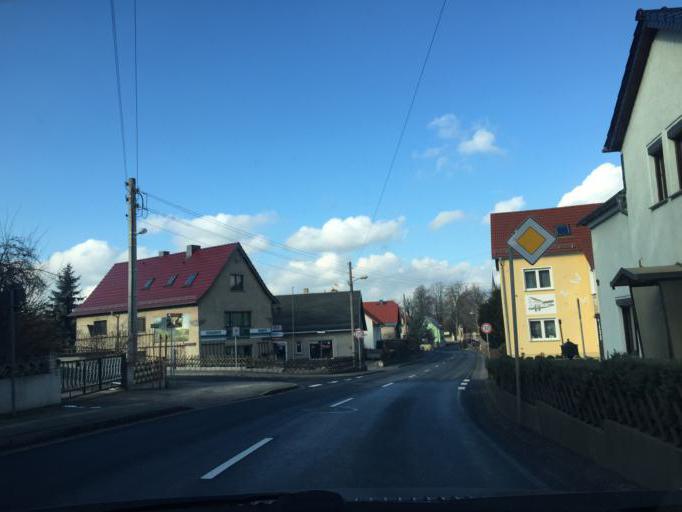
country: DE
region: Saxony
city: Schonfeld
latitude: 51.3016
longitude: 13.7099
